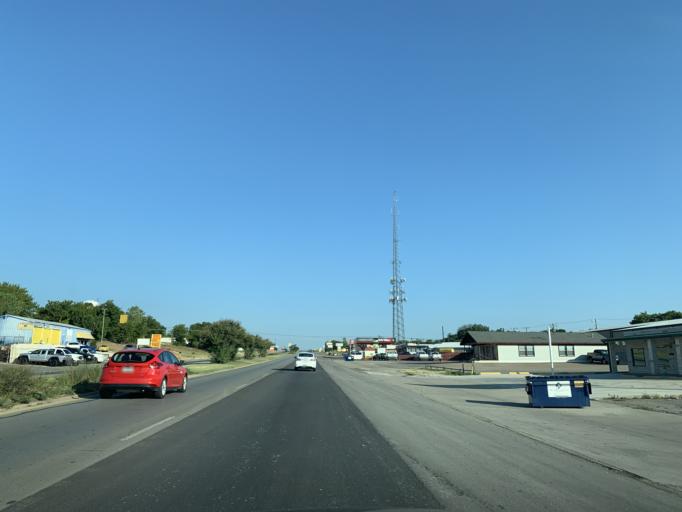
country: US
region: Texas
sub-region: Tarrant County
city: Sansom Park
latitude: 32.7999
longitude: -97.4064
